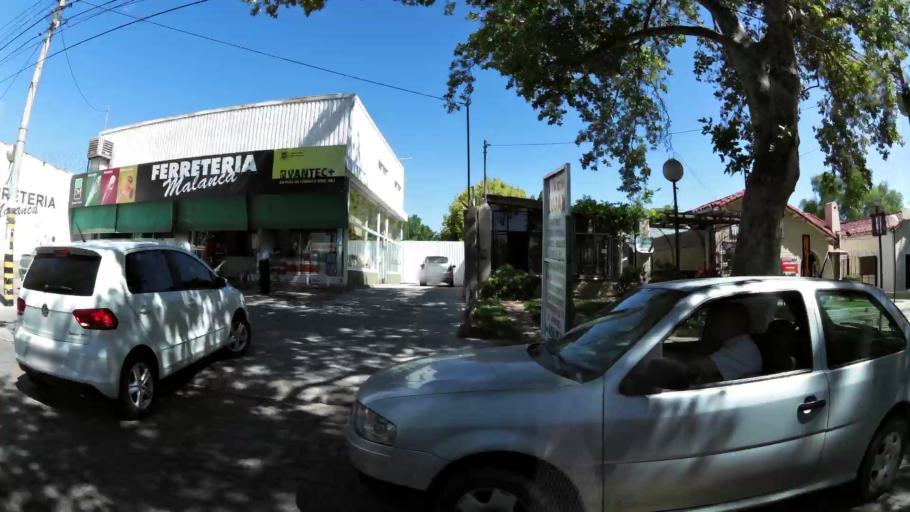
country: AR
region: Mendoza
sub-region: Departamento de Godoy Cruz
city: Godoy Cruz
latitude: -32.9632
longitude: -68.8536
